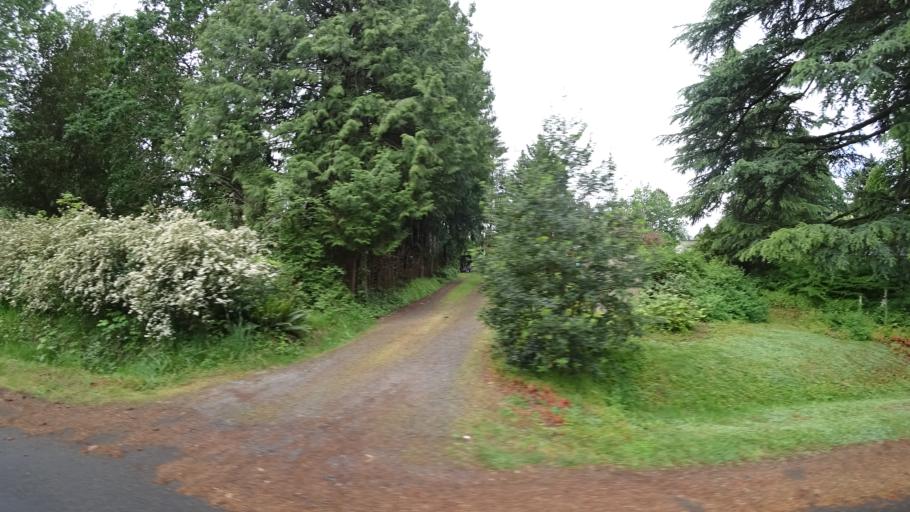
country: US
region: Oregon
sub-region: Washington County
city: Garden Home-Whitford
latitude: 45.4672
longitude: -122.7624
